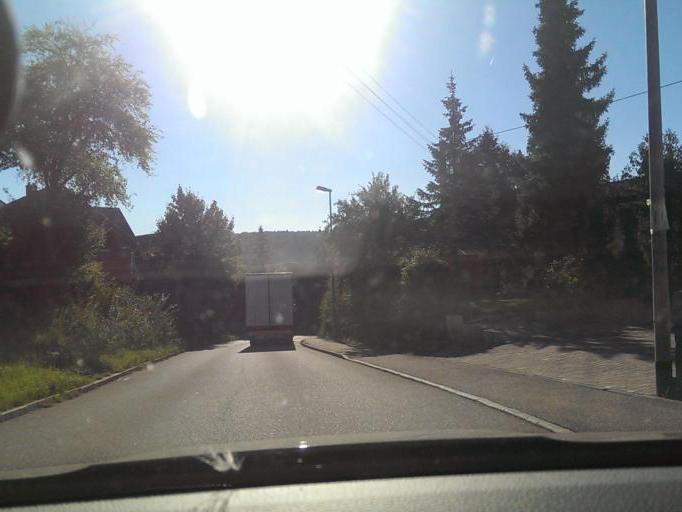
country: DE
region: Baden-Wuerttemberg
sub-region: Karlsruhe Region
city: Heimsheim
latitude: 48.8069
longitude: 8.8578
